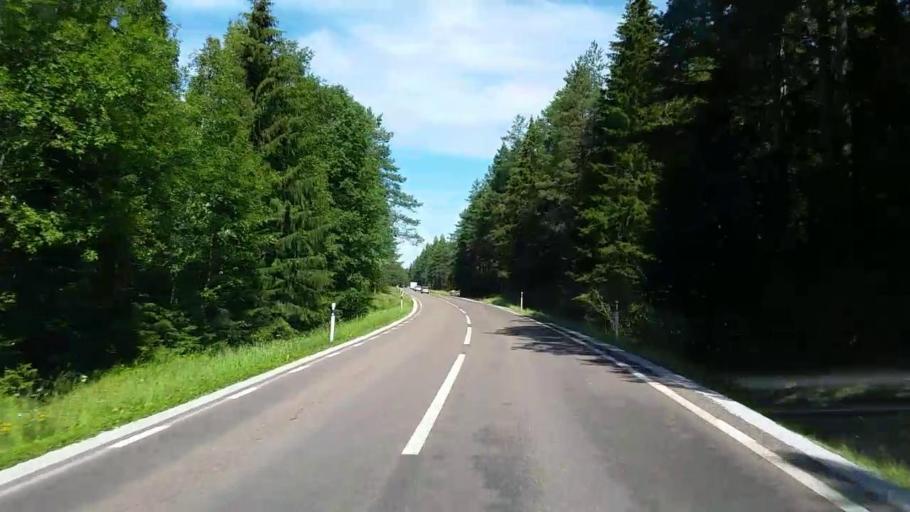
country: SE
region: Dalarna
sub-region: Rattviks Kommun
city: Raettvik
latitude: 60.9110
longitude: 15.2001
